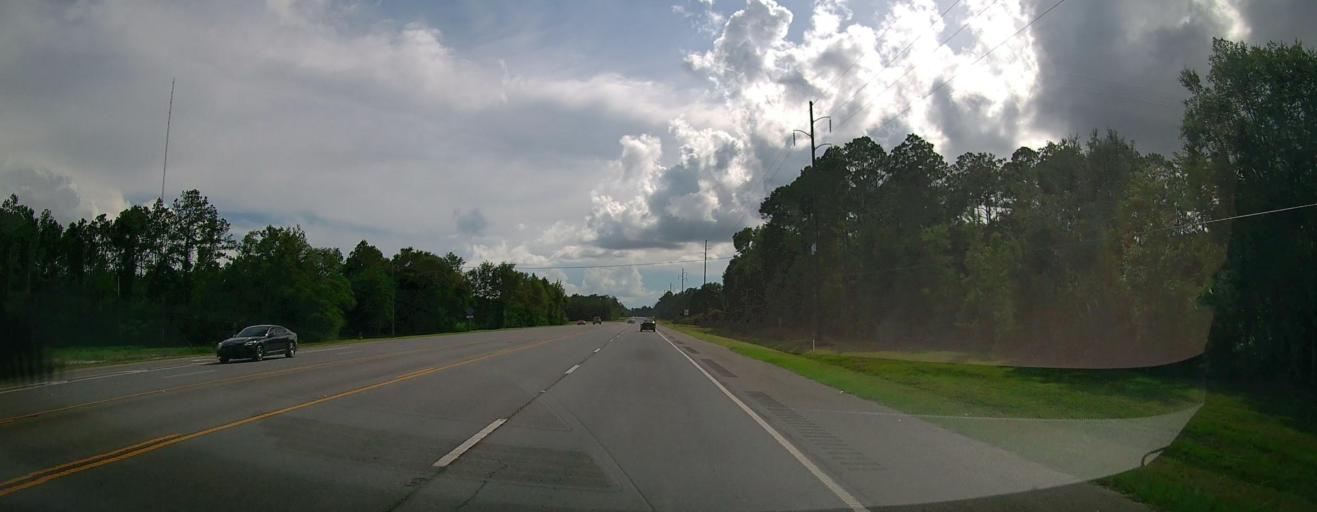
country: US
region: Georgia
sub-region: Wayne County
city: Jesup
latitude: 31.5987
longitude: -81.9344
